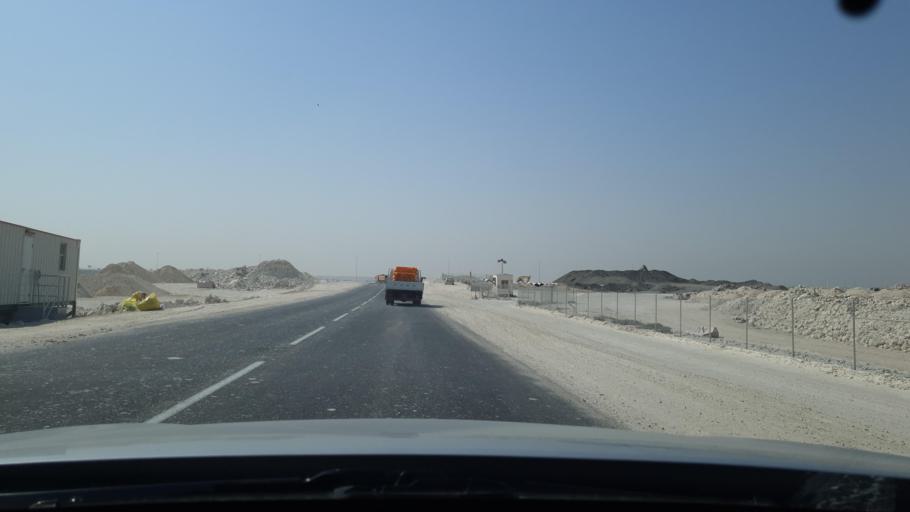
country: QA
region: Baladiyat ad Dawhah
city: Doha
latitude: 25.2281
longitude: 51.5211
